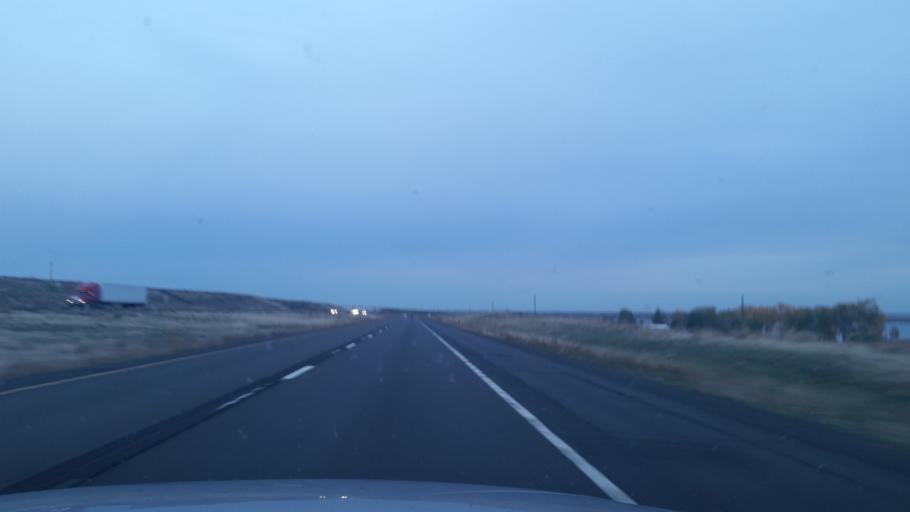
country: US
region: Washington
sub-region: Adams County
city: Ritzville
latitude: 47.2541
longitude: -118.0929
